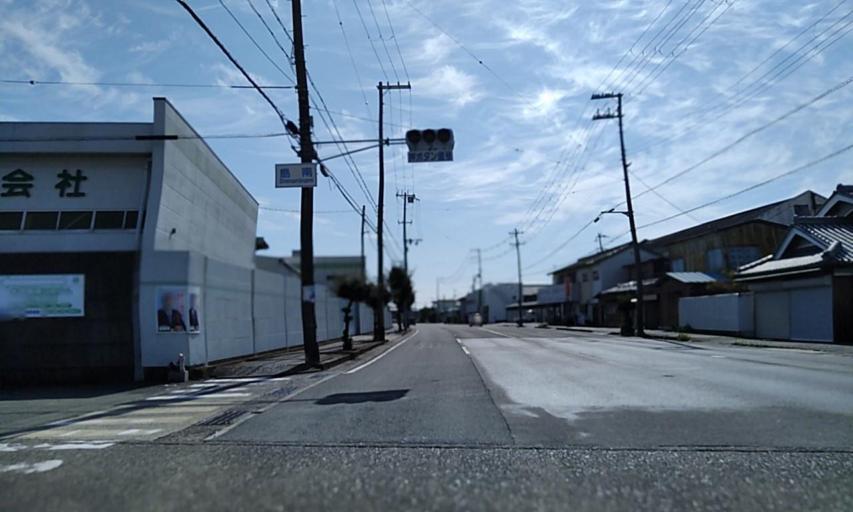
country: JP
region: Wakayama
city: Gobo
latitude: 33.8945
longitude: 135.1622
